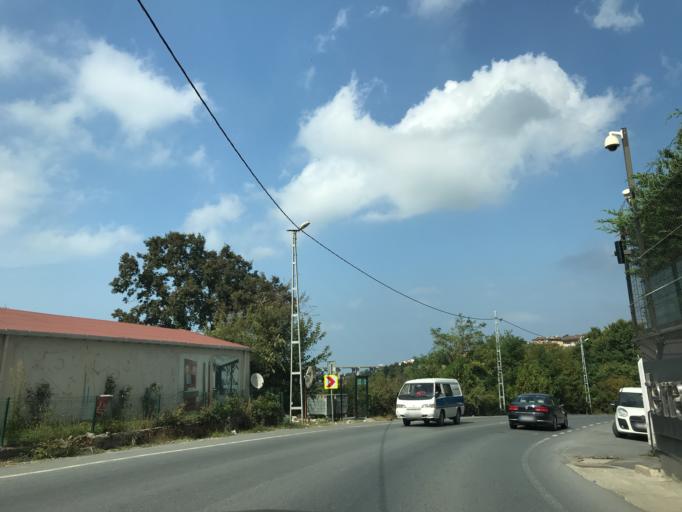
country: TR
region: Istanbul
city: Arikoey
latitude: 41.2150
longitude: 29.0341
